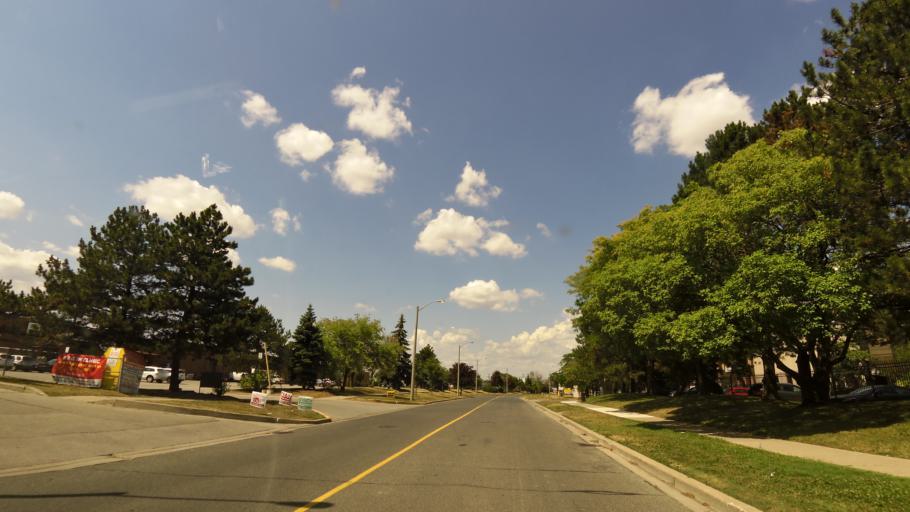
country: CA
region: Ontario
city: Etobicoke
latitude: 43.7409
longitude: -79.6037
